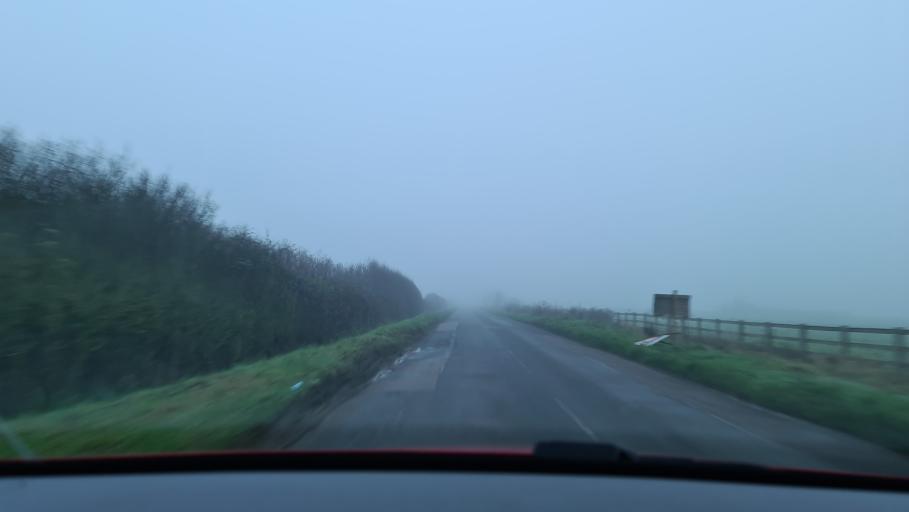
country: GB
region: England
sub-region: Buckinghamshire
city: Waddesdon
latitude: 51.8582
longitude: -0.8708
